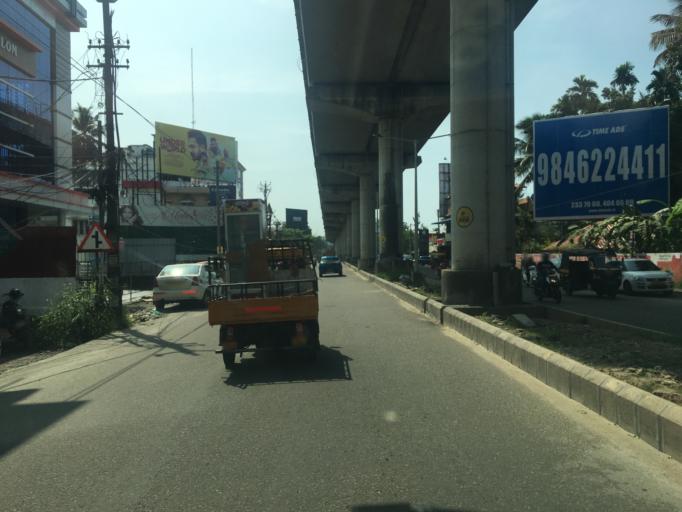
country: IN
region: Kerala
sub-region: Ernakulam
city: Cochin
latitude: 9.9683
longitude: 76.3145
